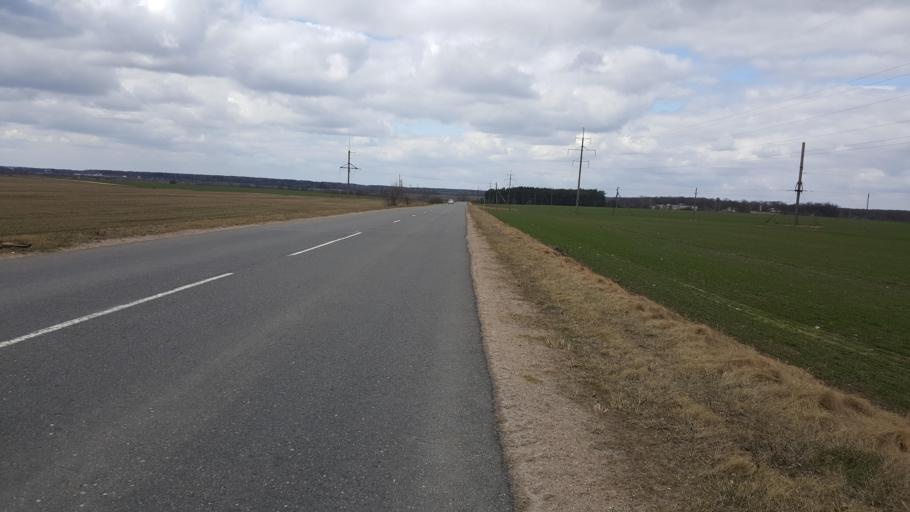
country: BY
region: Brest
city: Kamyanyets
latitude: 52.3793
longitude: 23.6697
